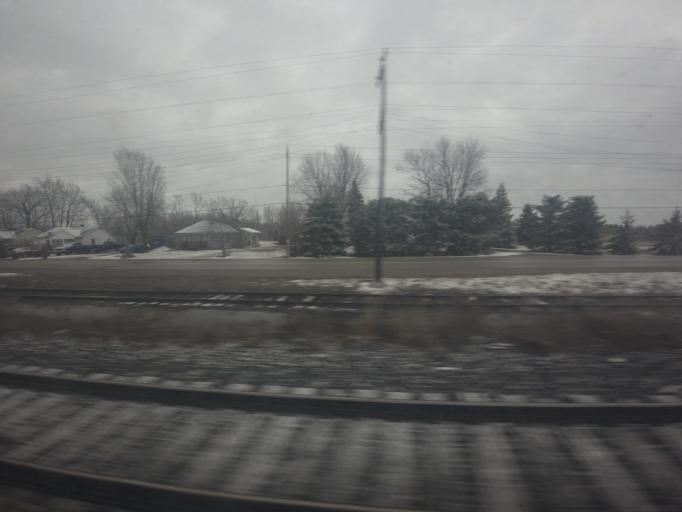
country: CA
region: Ontario
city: Gananoque
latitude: 44.3684
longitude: -76.1581
